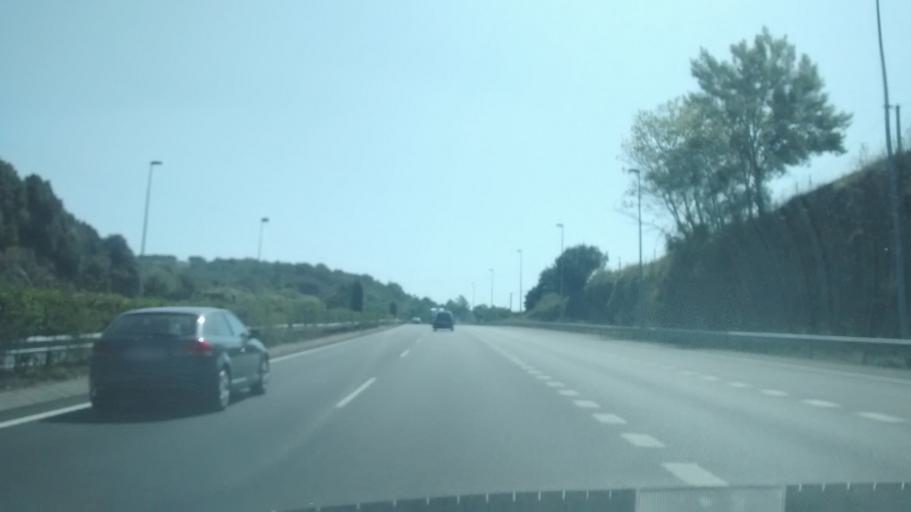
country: ES
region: Cantabria
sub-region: Provincia de Cantabria
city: Laredo
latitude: 43.4039
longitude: -3.4093
